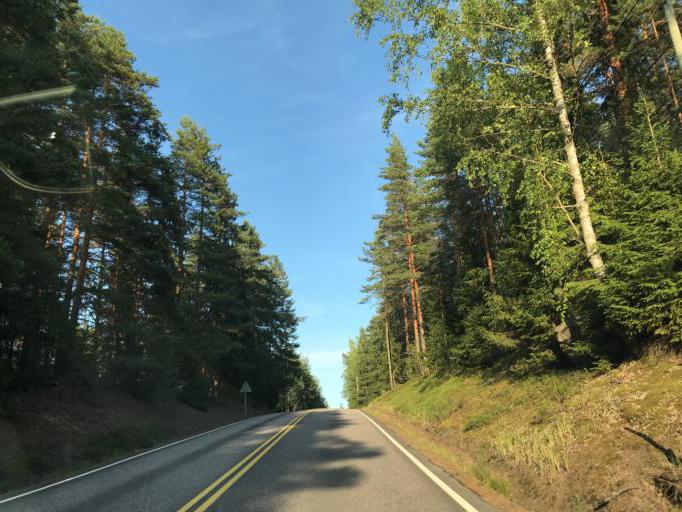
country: FI
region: Uusimaa
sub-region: Helsinki
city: Vihti
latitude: 60.4164
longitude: 24.4160
